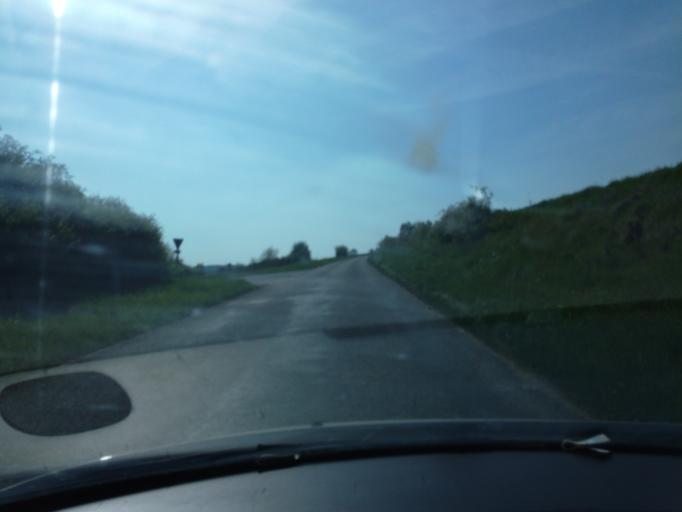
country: FR
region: Picardie
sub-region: Departement de la Somme
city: Quevauvillers
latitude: 49.8325
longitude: 2.0438
